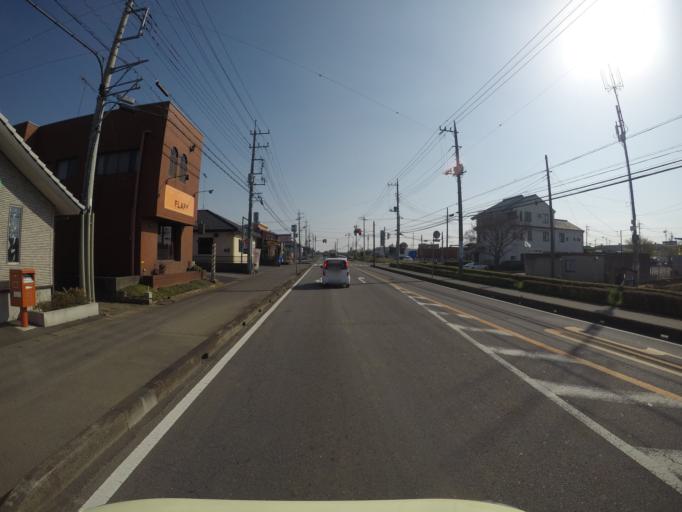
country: JP
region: Ibaraki
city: Yuki
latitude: 36.2725
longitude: 139.8786
